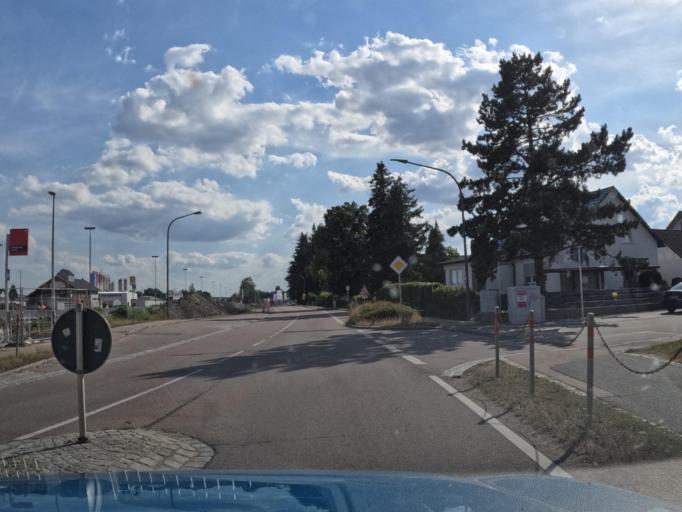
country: DE
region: Bavaria
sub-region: Upper Palatinate
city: Schwarzenfeld
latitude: 49.3934
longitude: 12.1308
